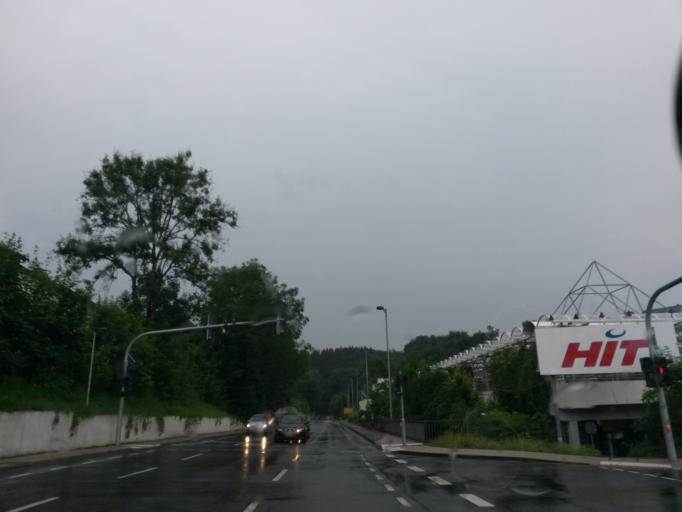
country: DE
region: North Rhine-Westphalia
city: Meinerzhagen
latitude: 51.1094
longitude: 7.6393
